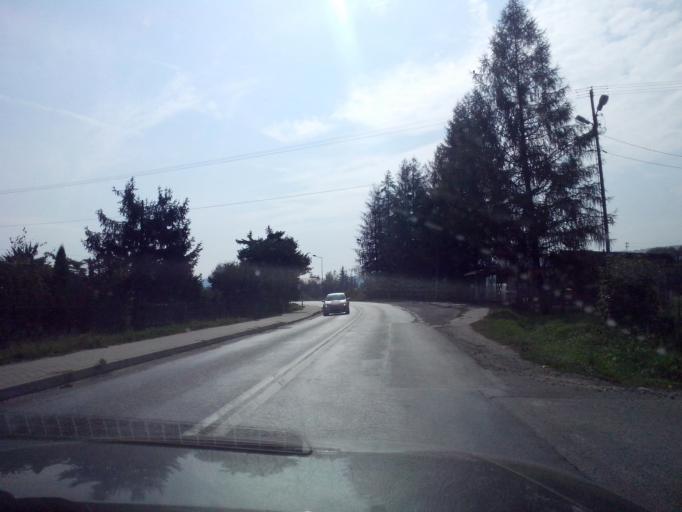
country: PL
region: Subcarpathian Voivodeship
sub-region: Powiat strzyzowski
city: Czudec
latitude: 49.9397
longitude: 21.8470
